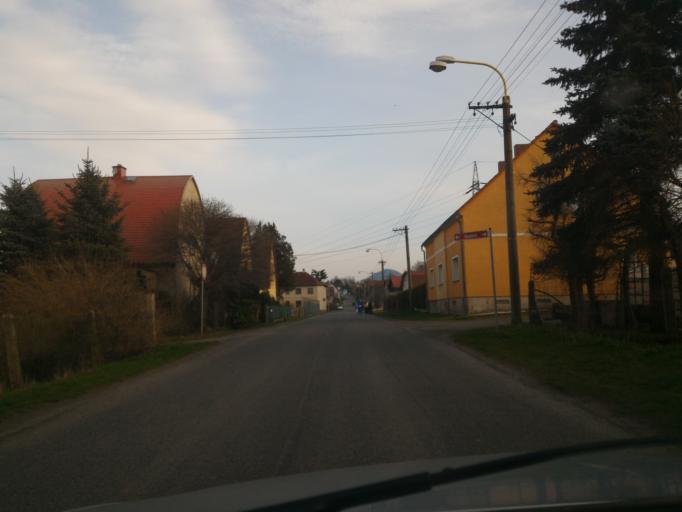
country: CZ
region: Ustecky
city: Varnsdorf
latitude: 50.9048
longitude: 14.6153
